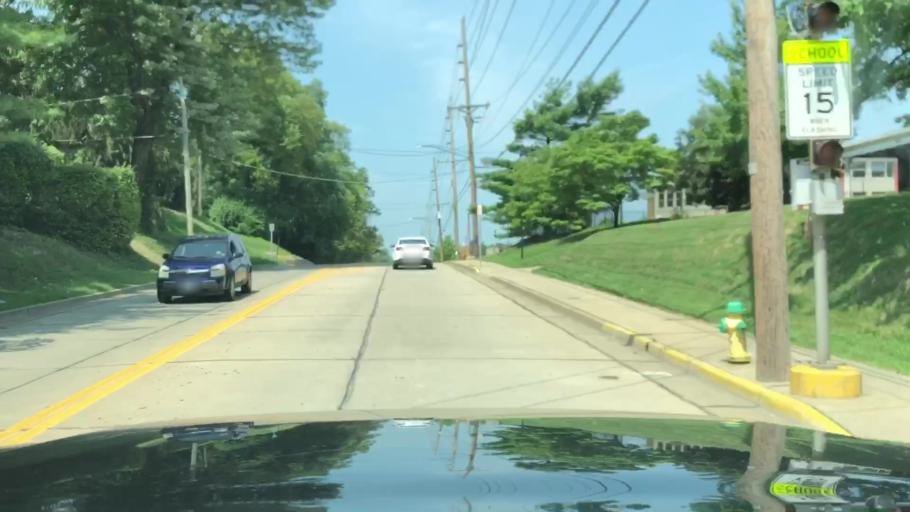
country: US
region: Missouri
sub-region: Saint Charles County
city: Saint Charles
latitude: 38.7909
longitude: -90.4961
